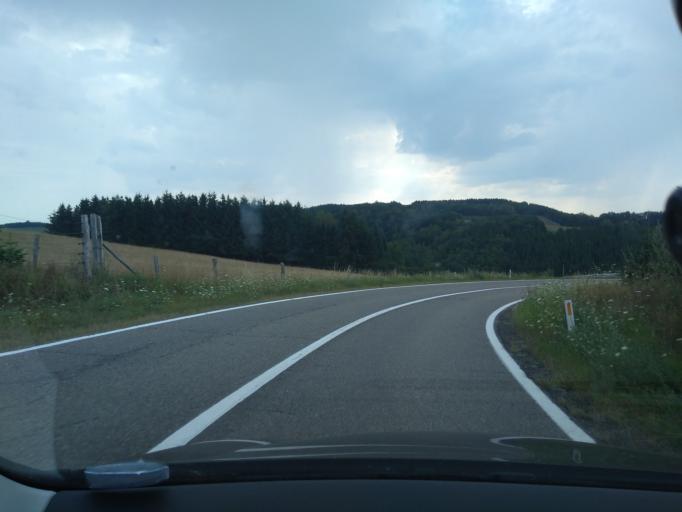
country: BE
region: Wallonia
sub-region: Province du Luxembourg
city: Bertogne
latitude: 50.0627
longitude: 5.6290
